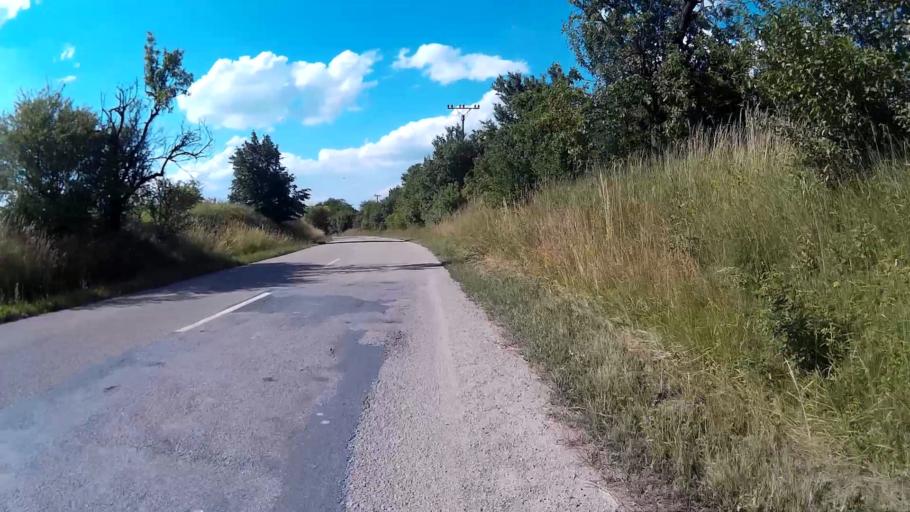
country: CZ
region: South Moravian
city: Sitborice
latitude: 49.0061
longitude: 16.7795
